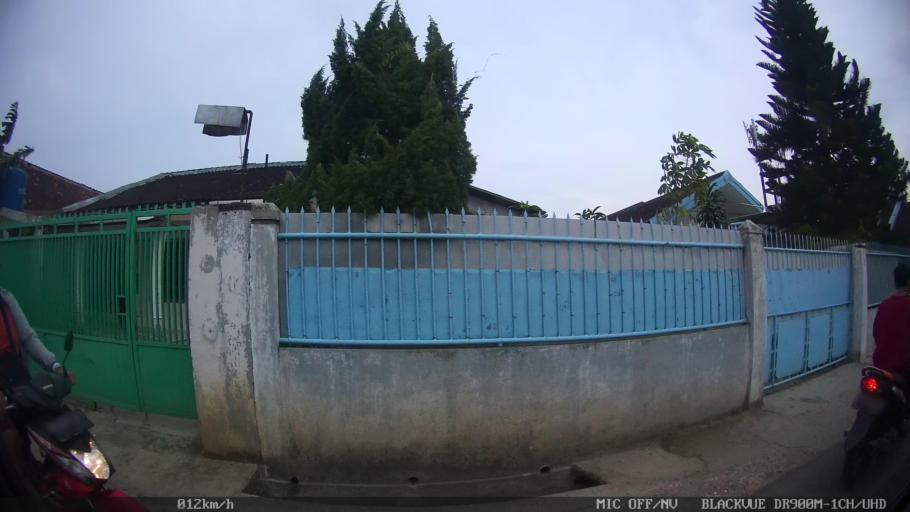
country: ID
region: Lampung
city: Kedaton
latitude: -5.4037
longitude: 105.2695
